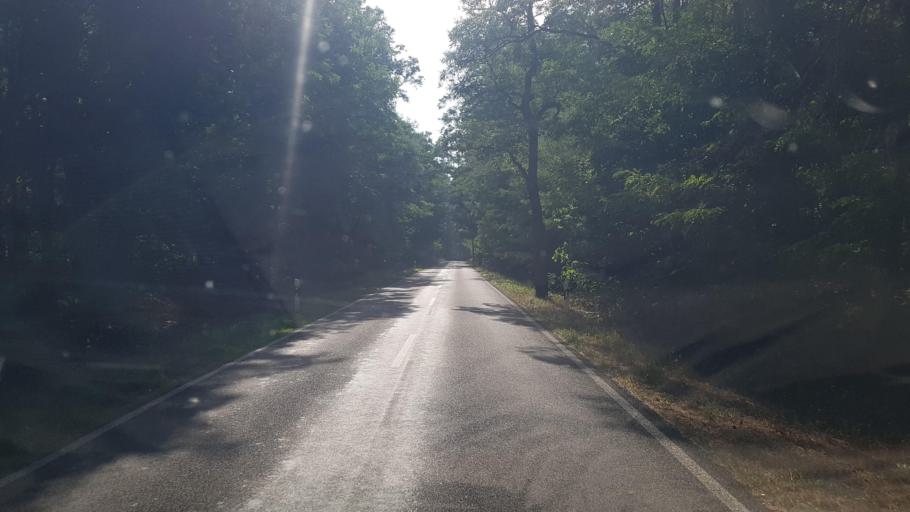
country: DE
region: Brandenburg
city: Dahme
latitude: 51.9508
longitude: 13.4061
